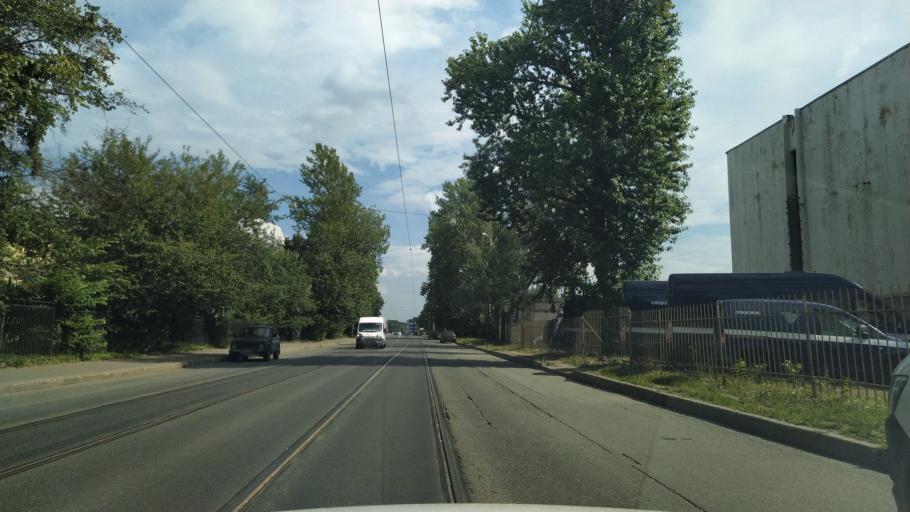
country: RU
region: Leningrad
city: Finlyandskiy
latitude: 59.9651
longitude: 30.3927
